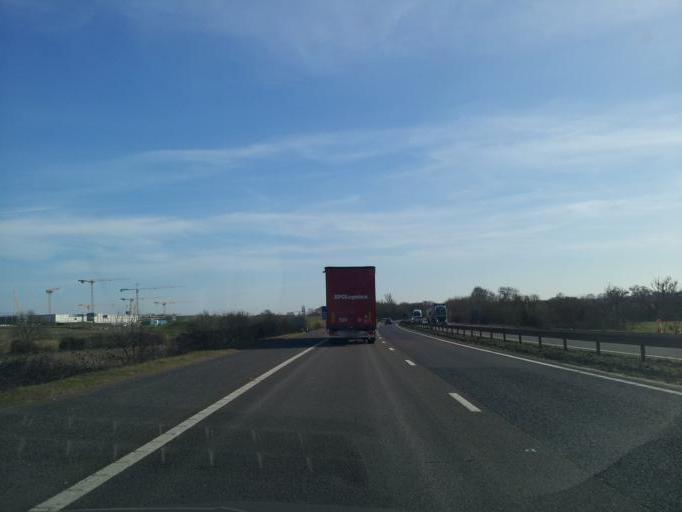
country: GB
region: England
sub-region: Cambridgeshire
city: Girton
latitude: 52.2243
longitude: 0.0770
